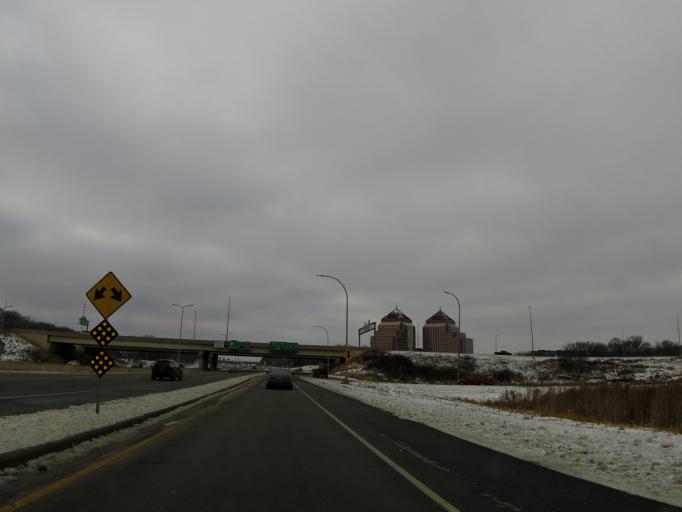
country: US
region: Minnesota
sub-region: Hennepin County
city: Minnetonka Mills
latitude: 44.9712
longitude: -93.4582
